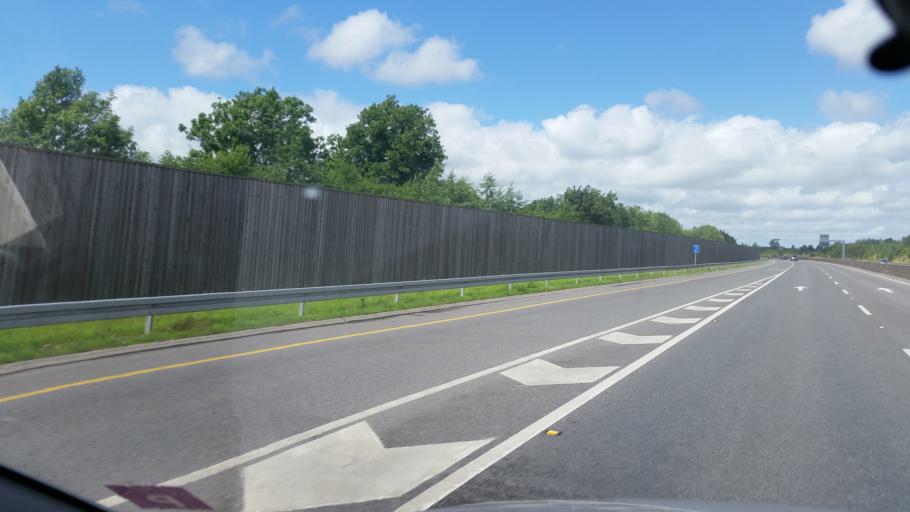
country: IE
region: Leinster
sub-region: An Mhi
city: Dunboyne
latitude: 53.4401
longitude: -6.4699
